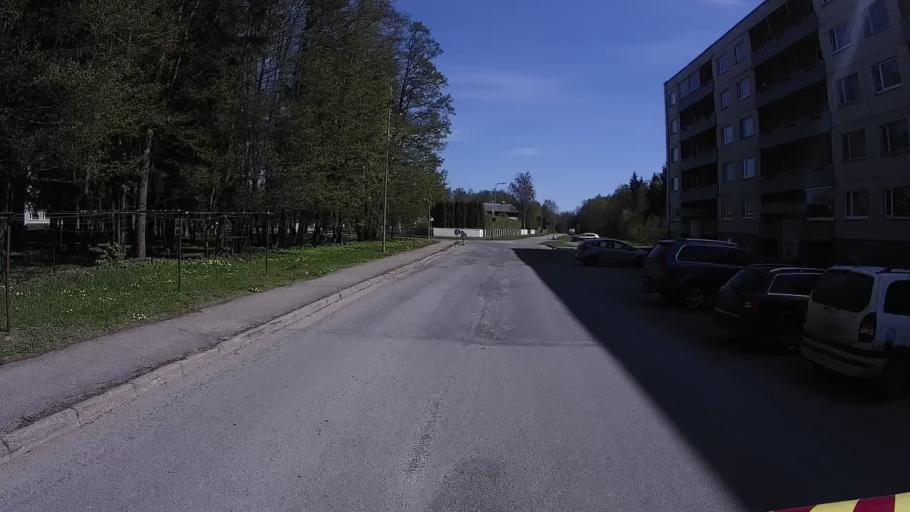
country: EE
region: Laeaene
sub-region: Haapsalu linn
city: Haapsalu
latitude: 58.9346
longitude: 23.5599
